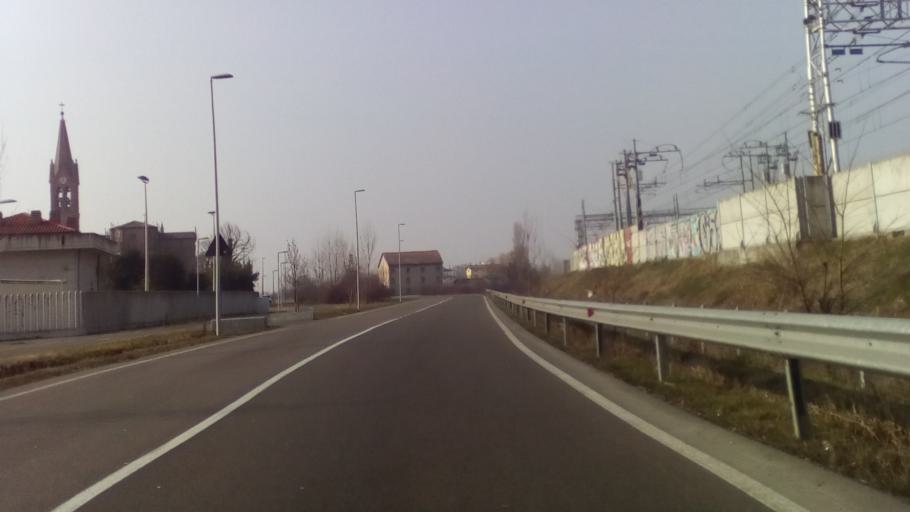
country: IT
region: Emilia-Romagna
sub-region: Provincia di Modena
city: Modena
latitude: 44.6592
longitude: 10.9139
